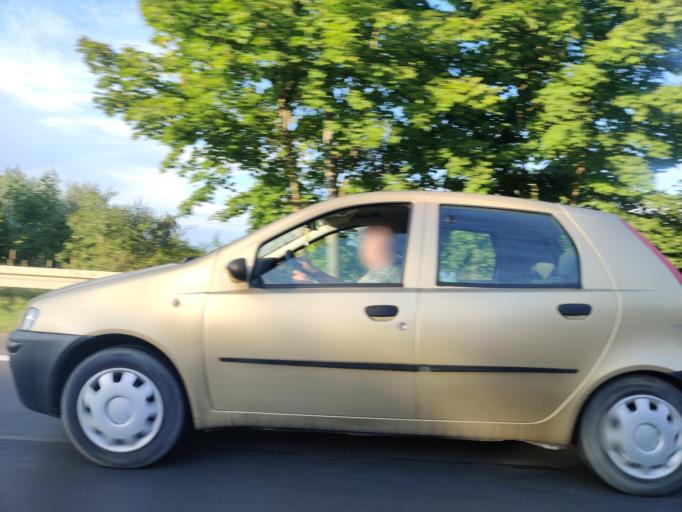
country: PL
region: Greater Poland Voivodeship
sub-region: Konin
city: Konin
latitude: 52.2072
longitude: 18.2664
